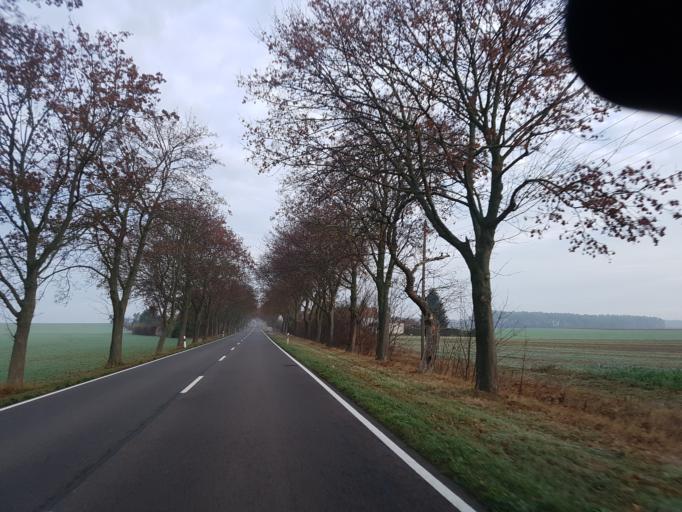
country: DE
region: Saxony-Anhalt
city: Kropstadt
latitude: 51.9687
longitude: 12.7559
